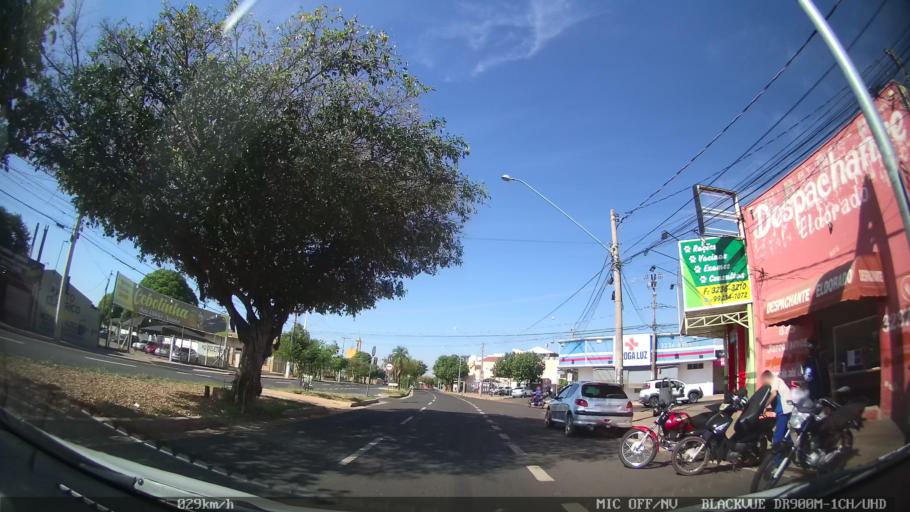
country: BR
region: Sao Paulo
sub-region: Sao Jose Do Rio Preto
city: Sao Jose do Rio Preto
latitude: -20.7833
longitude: -49.3957
